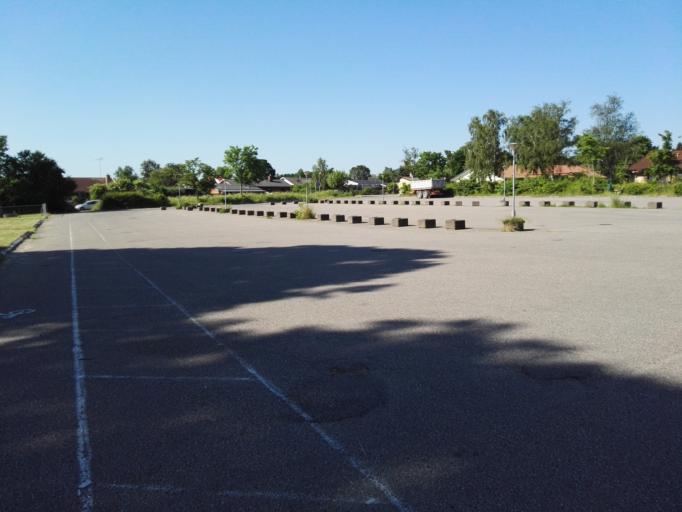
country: DK
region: Zealand
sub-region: Lejre Kommune
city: Ejby
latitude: 55.7072
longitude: 11.8979
